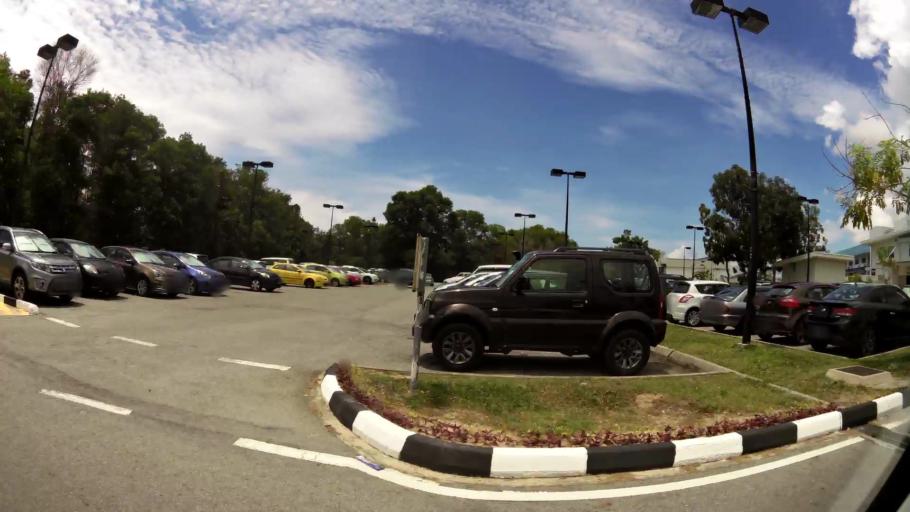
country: BN
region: Brunei and Muara
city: Bandar Seri Begawan
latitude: 4.9779
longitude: 114.8996
